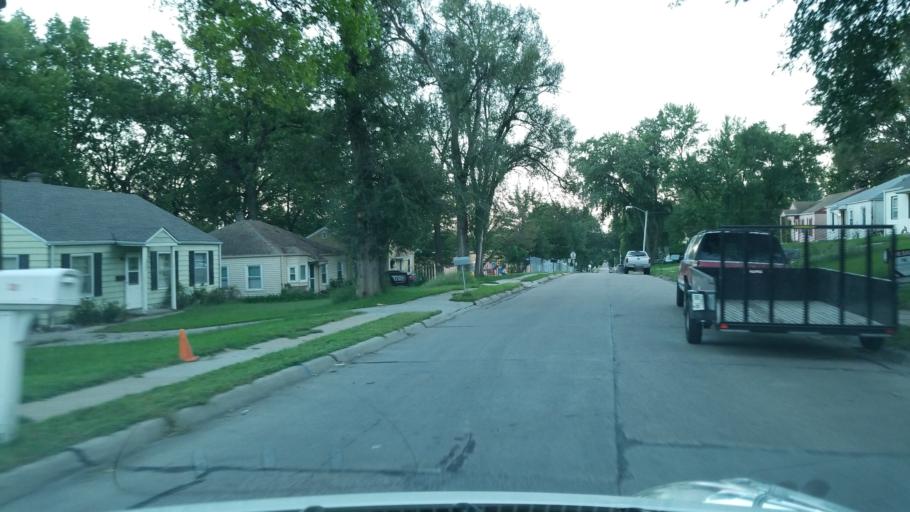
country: US
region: Nebraska
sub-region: Sarpy County
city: Bellevue
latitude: 41.1395
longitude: -95.9003
